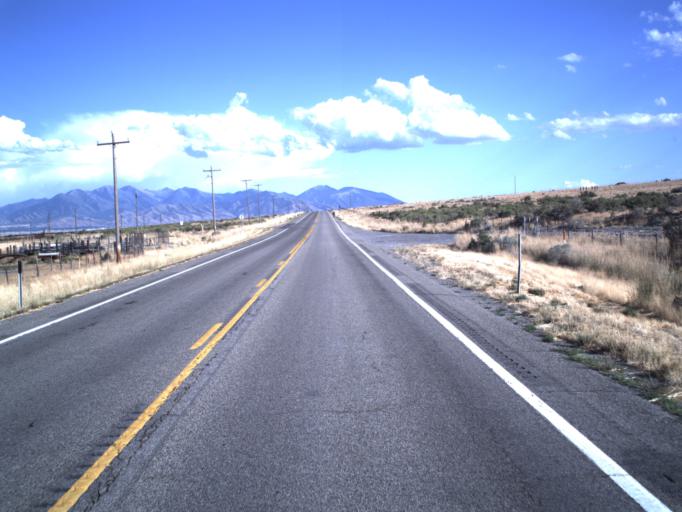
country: US
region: Utah
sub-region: Tooele County
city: Grantsville
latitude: 40.6398
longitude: -112.5233
